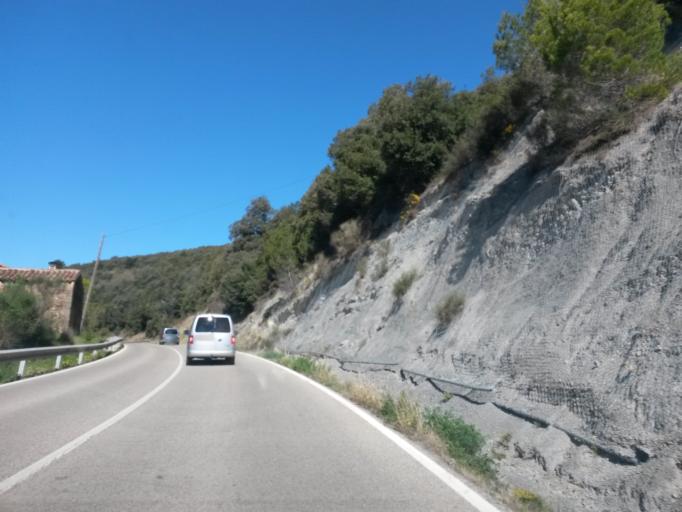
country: ES
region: Catalonia
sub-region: Provincia de Girona
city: Santa Pau
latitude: 42.1478
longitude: 2.5515
